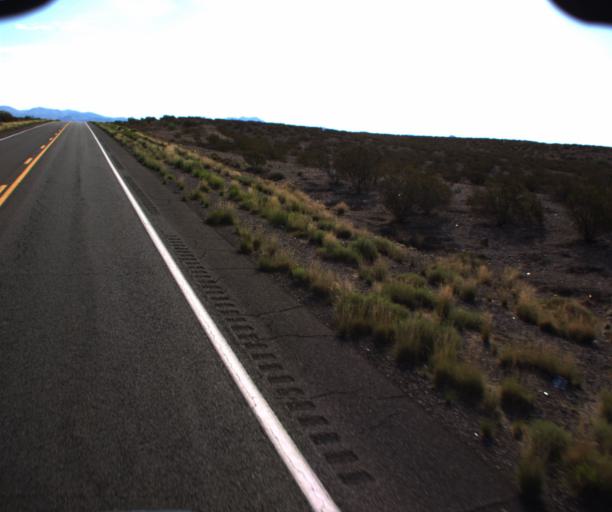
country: US
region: Arizona
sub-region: Graham County
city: Safford
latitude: 32.7957
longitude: -109.5402
